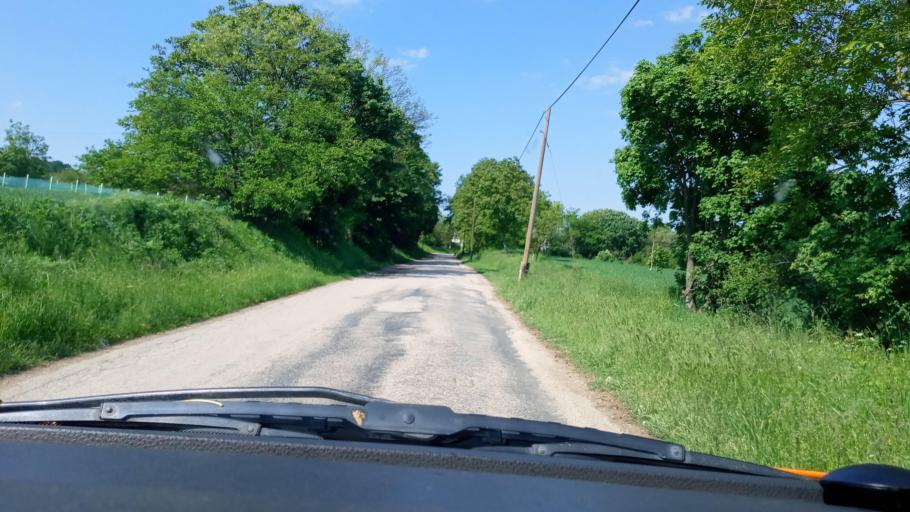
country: HU
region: Baranya
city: Harkany
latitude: 45.9048
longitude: 18.2542
